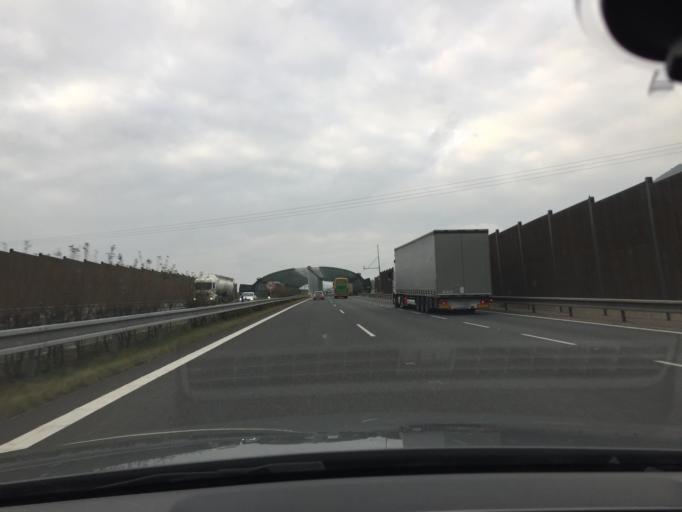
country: CZ
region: Ustecky
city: Lovosice
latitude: 50.5115
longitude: 14.0268
